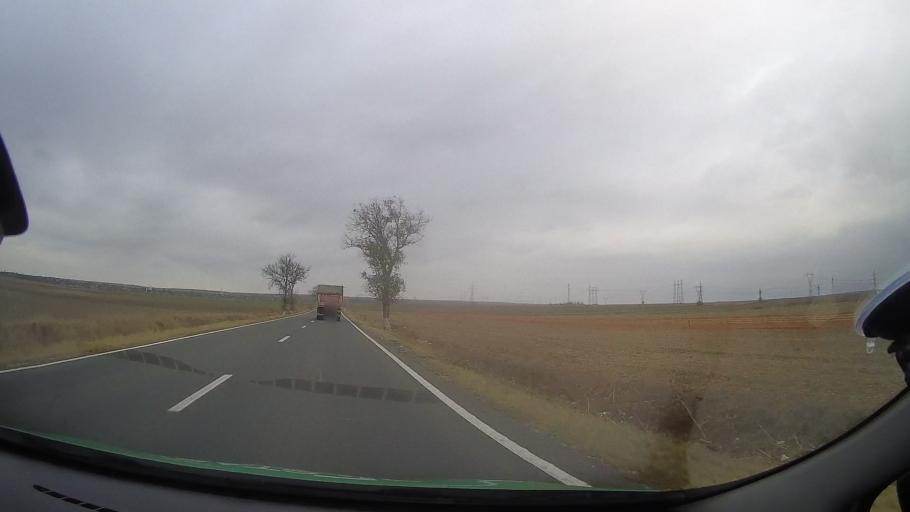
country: RO
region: Constanta
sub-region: Comuna Castelu
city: Castelu
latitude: 44.2526
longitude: 28.3544
